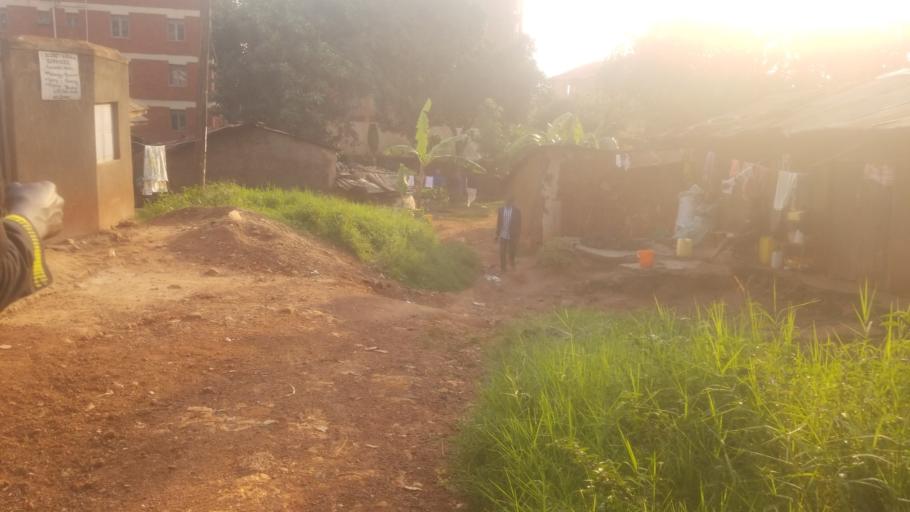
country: UG
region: Central Region
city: Kampala Central Division
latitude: 0.3373
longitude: 32.5623
